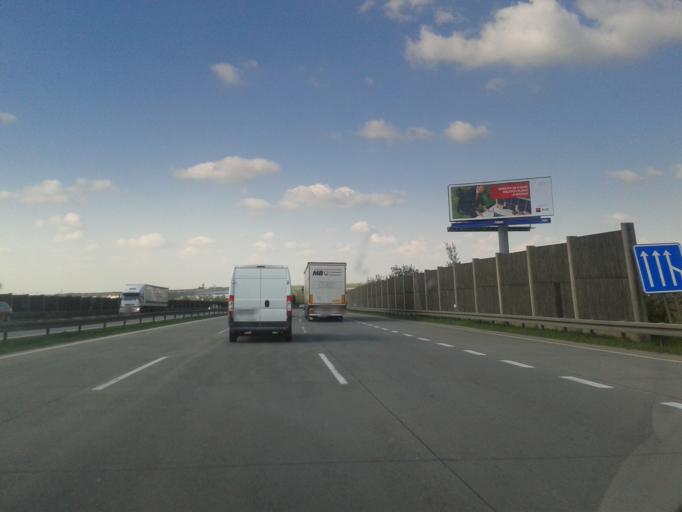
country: CZ
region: Central Bohemia
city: Hostivice
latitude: 50.0588
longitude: 14.2768
